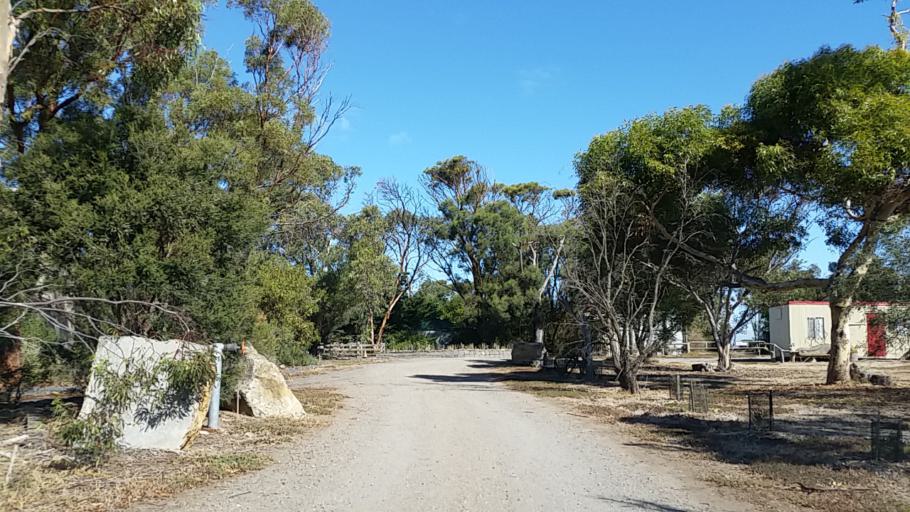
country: AU
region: South Australia
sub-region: Onkaparinga
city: Aldinga
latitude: -35.2665
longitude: 138.4800
